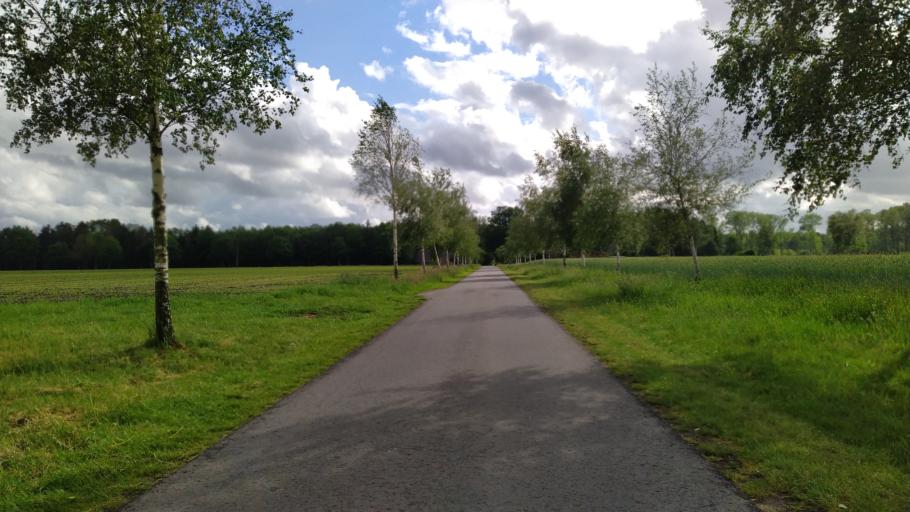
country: DE
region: Lower Saxony
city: Brest
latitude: 53.4365
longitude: 9.3563
